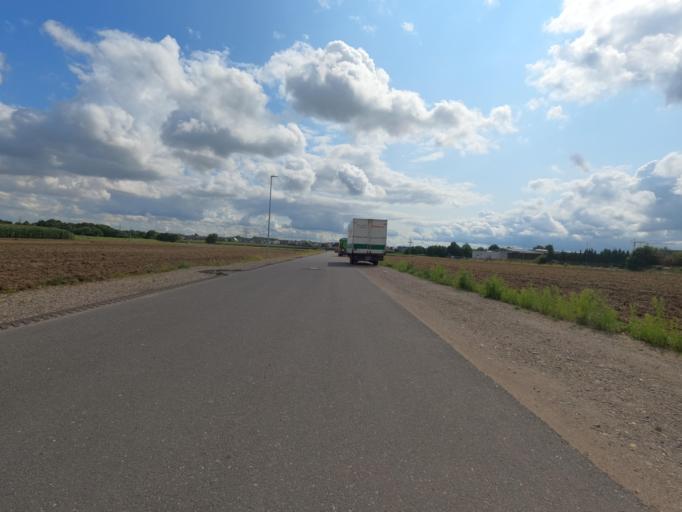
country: DE
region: North Rhine-Westphalia
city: Baesweiler
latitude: 50.9208
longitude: 6.1847
